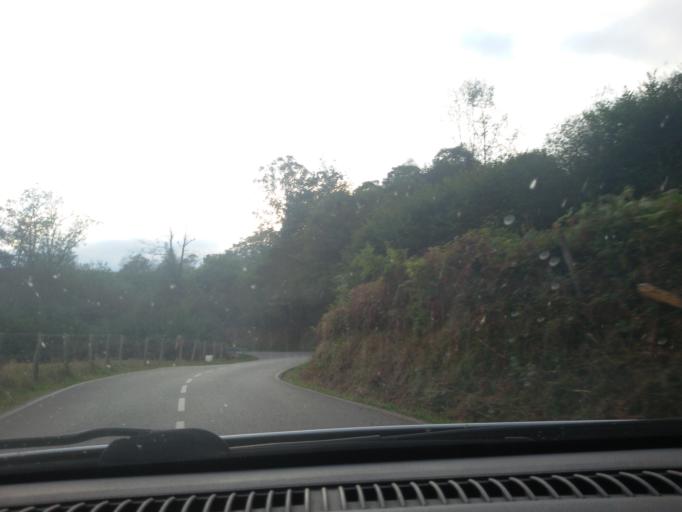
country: ES
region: Asturias
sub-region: Province of Asturias
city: Bimenes
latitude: 43.3359
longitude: -5.5800
